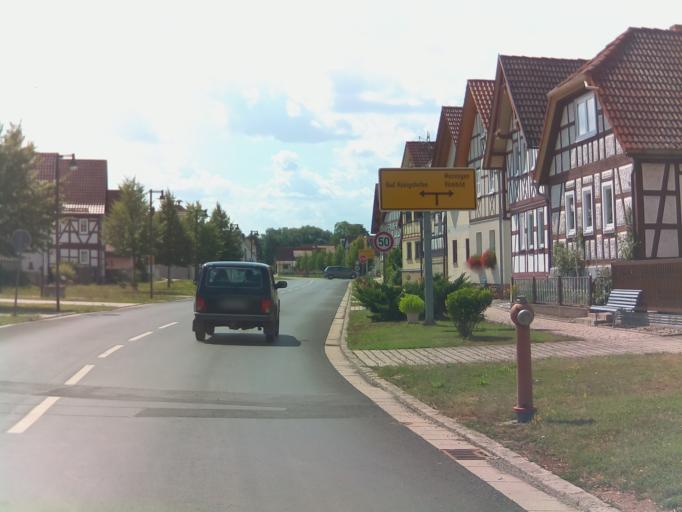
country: DE
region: Bavaria
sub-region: Regierungsbezirk Unterfranken
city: Trappstadt
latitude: 50.3499
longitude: 10.5719
